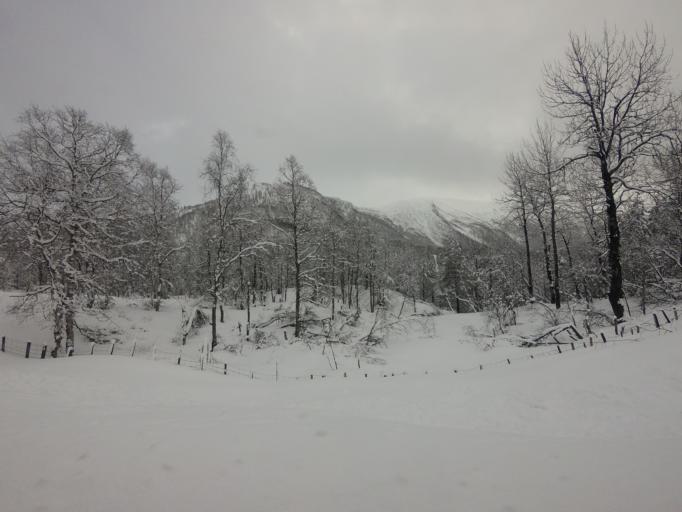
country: NO
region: Hordaland
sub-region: Ulvik
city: Ulvik
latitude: 60.6865
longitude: 6.8148
